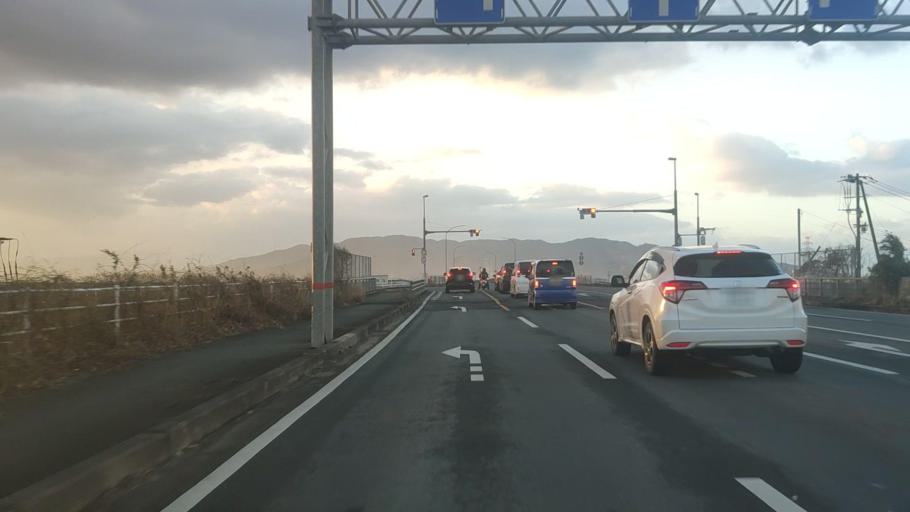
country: JP
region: Kumamoto
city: Uto
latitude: 32.7384
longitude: 130.7046
